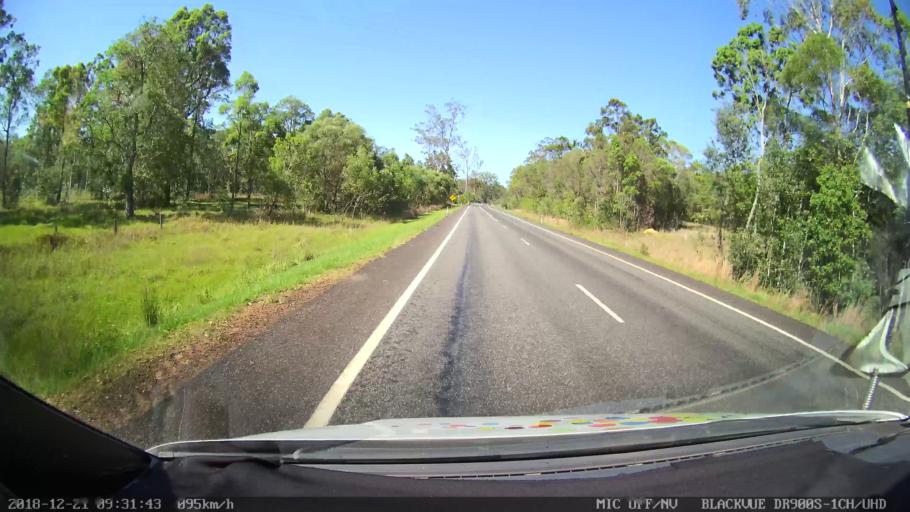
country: AU
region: New South Wales
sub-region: Clarence Valley
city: Maclean
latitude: -29.4630
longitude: 152.9856
